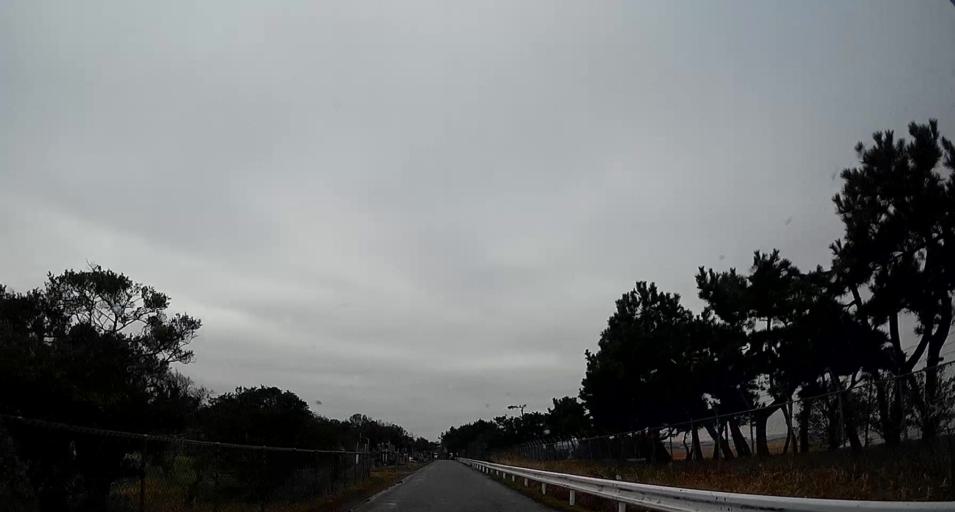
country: JP
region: Chiba
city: Kisarazu
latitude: 35.4062
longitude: 139.9136
